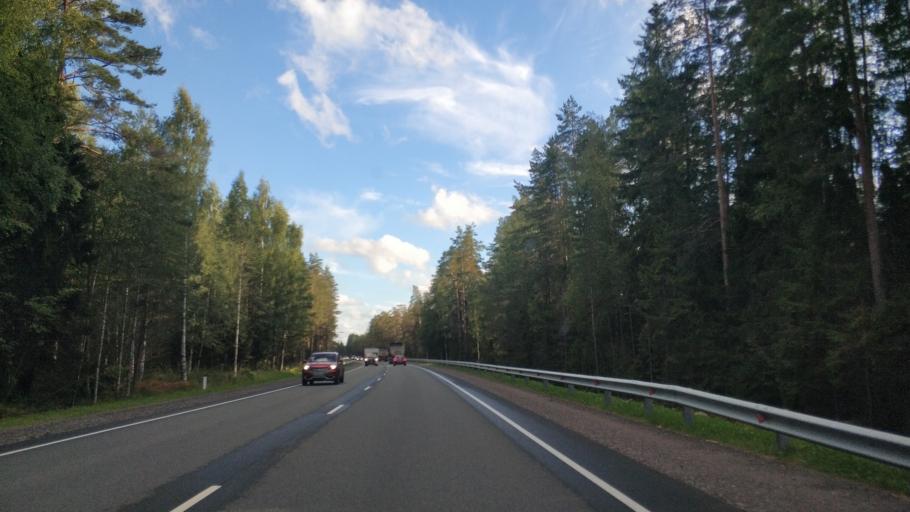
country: RU
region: Leningrad
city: Priozersk
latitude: 60.8926
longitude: 30.1596
